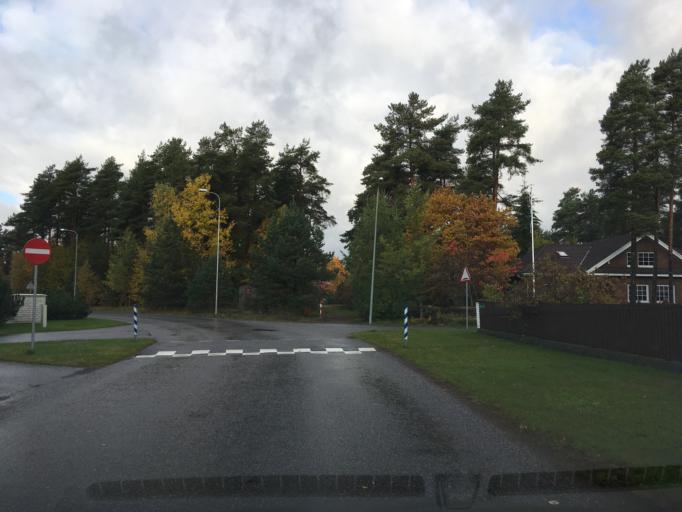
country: EE
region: Harju
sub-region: Saue vald
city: Laagri
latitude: 59.3601
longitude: 24.6054
